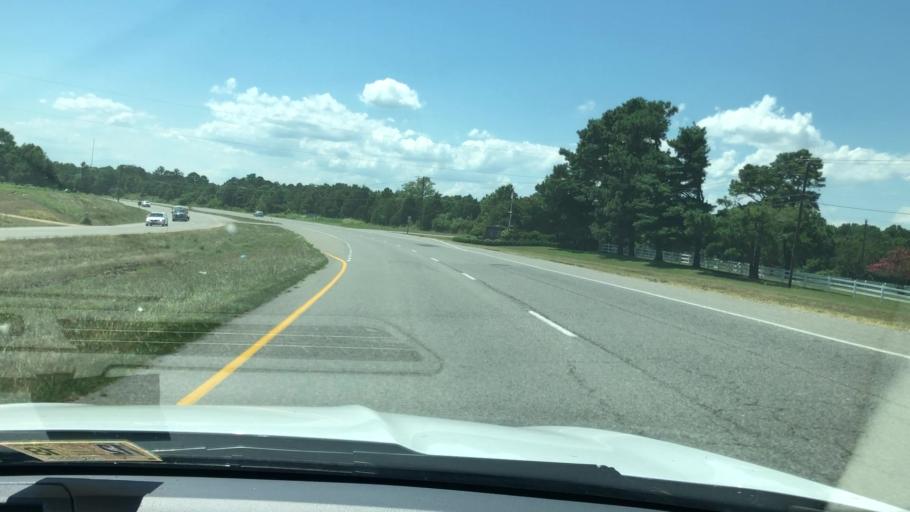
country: US
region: Virginia
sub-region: Middlesex County
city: Saluda
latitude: 37.6091
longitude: -76.5500
